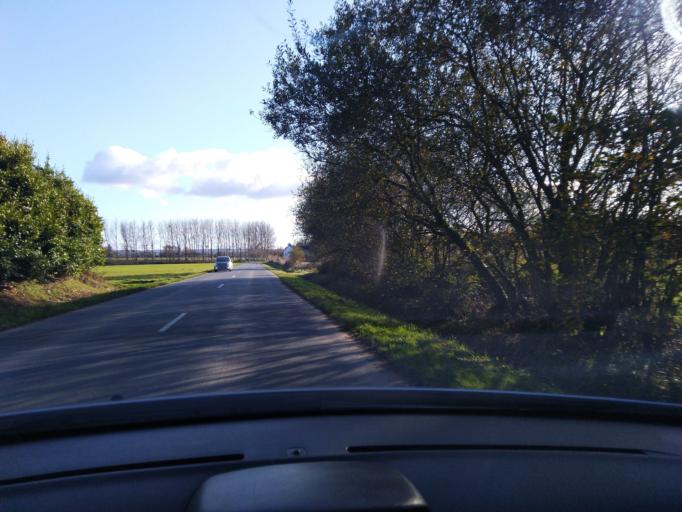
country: FR
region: Brittany
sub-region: Departement des Cotes-d'Armor
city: Plestin-les-Greves
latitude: 48.6292
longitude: -3.6155
